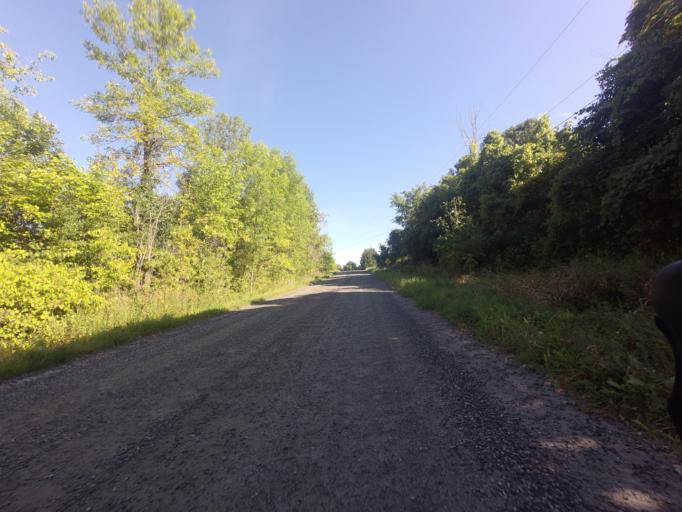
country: CA
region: Ontario
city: Perth
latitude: 44.9282
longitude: -76.3671
